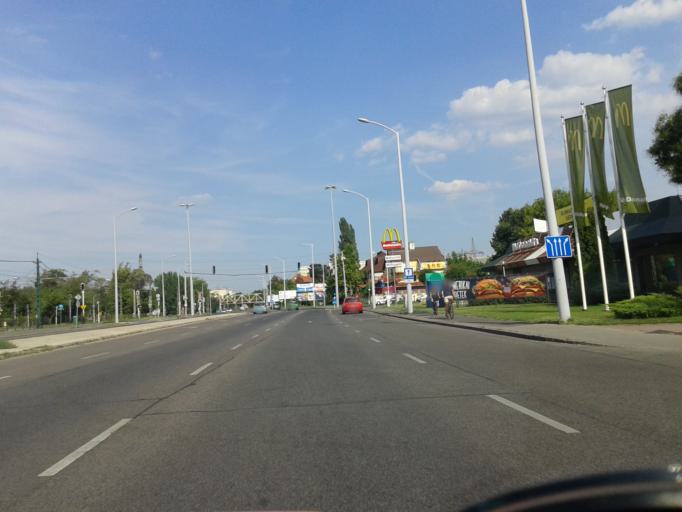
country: HU
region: Budapest
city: Budapest XVI. keruelet
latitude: 47.5048
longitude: 19.1511
